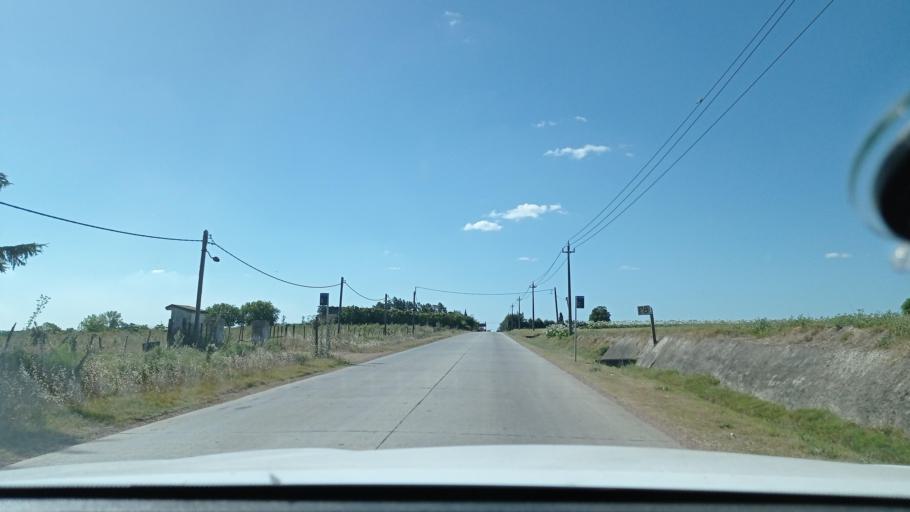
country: UY
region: Canelones
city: La Paz
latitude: -34.7766
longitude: -56.2581
